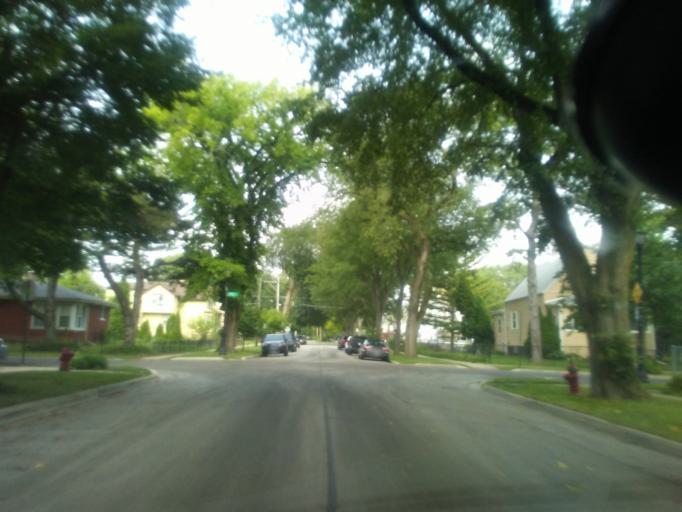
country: US
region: Illinois
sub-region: Cook County
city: Evanston
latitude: 42.0538
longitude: -87.7017
